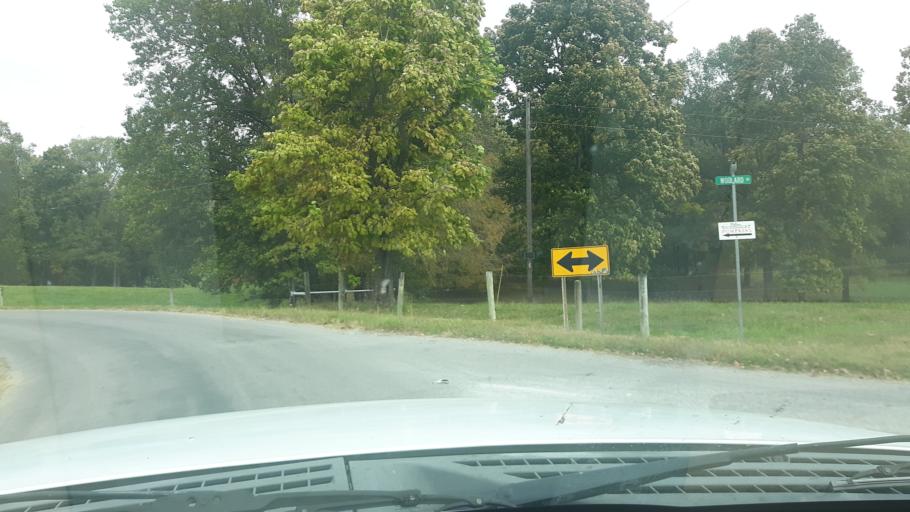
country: US
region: Illinois
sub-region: Saline County
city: Eldorado
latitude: 37.8362
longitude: -88.4849
